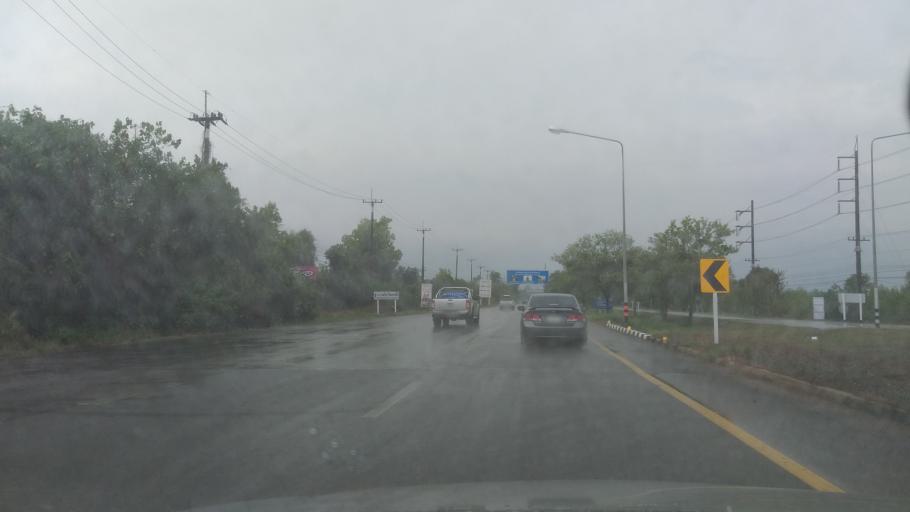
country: TH
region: Trat
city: Khao Saming
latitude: 12.3900
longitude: 102.3681
